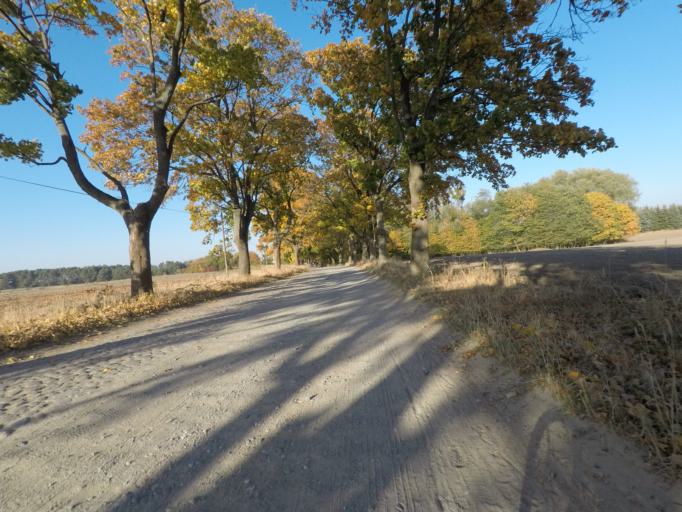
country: DE
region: Brandenburg
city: Biesenthal
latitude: 52.7705
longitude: 13.6396
